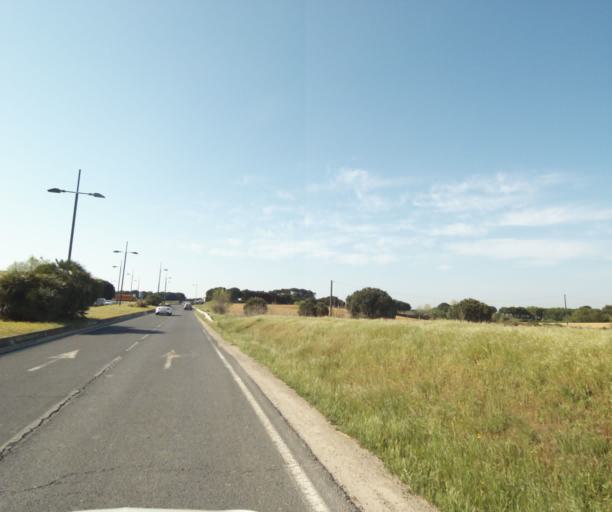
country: FR
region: Languedoc-Roussillon
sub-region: Departement de l'Herault
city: Castelnau-le-Lez
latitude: 43.6103
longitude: 3.9296
